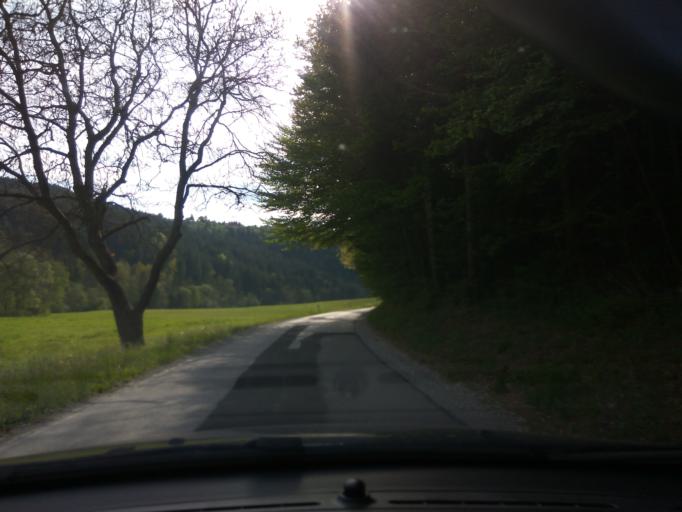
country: AT
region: Styria
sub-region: Politischer Bezirk Voitsberg
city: Voitsberg
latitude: 47.0305
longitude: 15.1233
